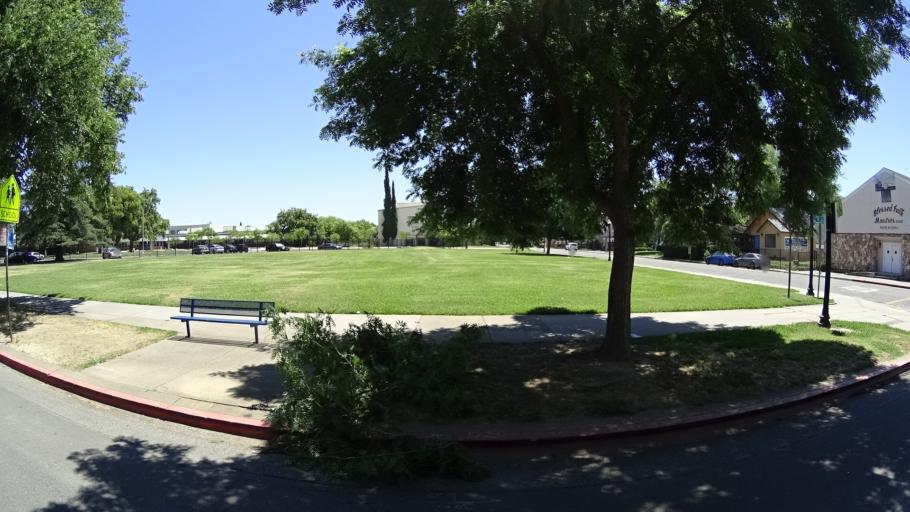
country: US
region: California
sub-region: Sacramento County
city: Sacramento
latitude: 38.5553
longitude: -121.4684
